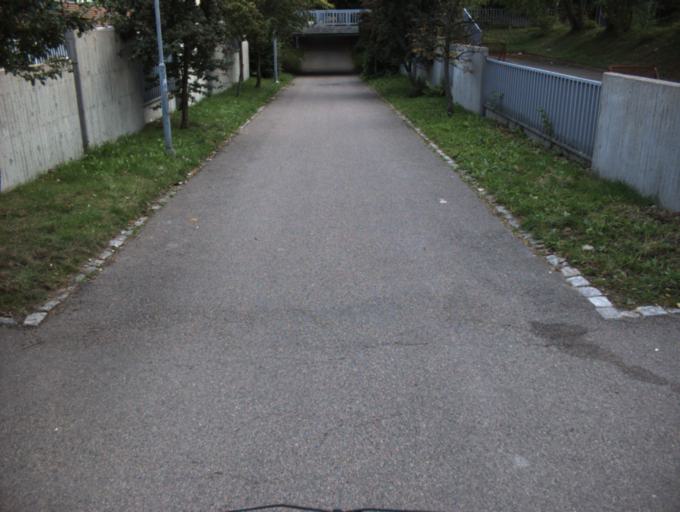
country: SE
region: Skane
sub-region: Helsingborg
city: Helsingborg
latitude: 56.0572
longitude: 12.7205
